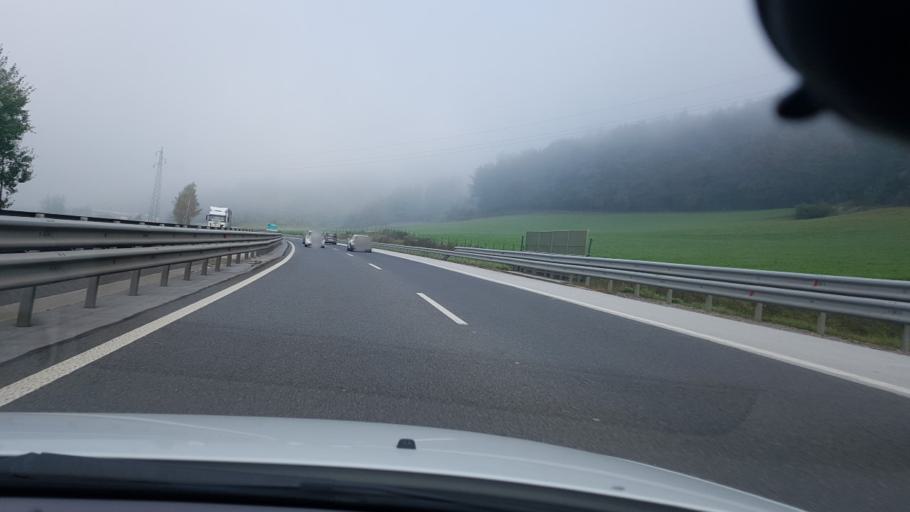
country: SI
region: Ivancna Gorica
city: Ivancna Gorica
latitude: 45.9442
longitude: 14.7788
